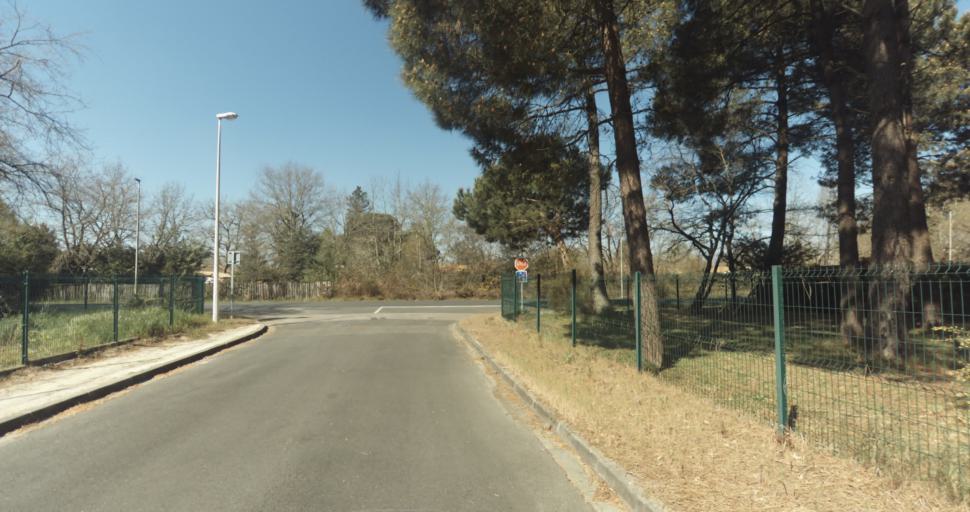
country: FR
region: Aquitaine
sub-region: Departement de la Gironde
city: Martignas-sur-Jalle
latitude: 44.8018
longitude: -0.7779
